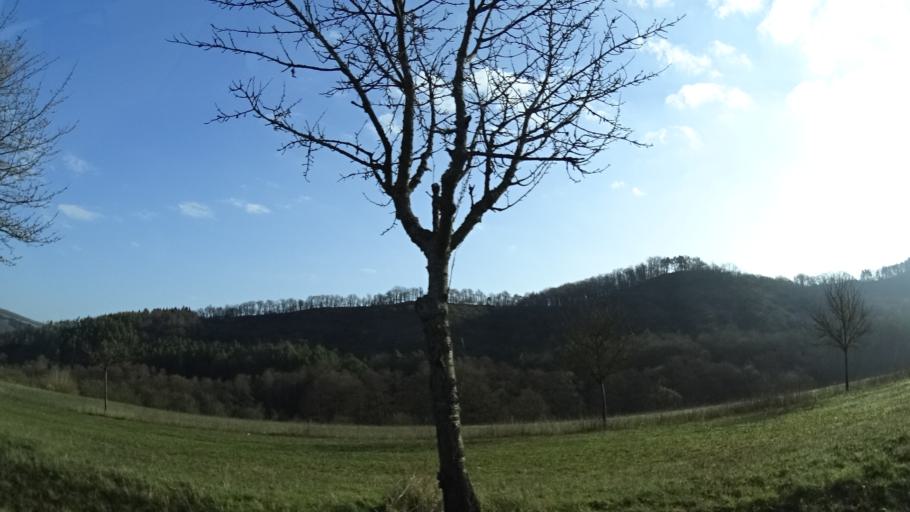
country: DE
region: Rheinland-Pfalz
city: Fischbach
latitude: 49.7340
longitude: 7.4106
